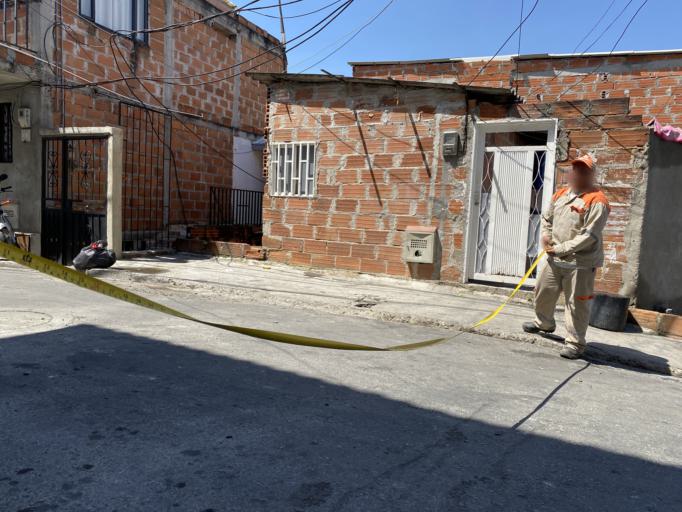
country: CO
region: Antioquia
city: Bello
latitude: 6.3011
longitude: -75.5468
